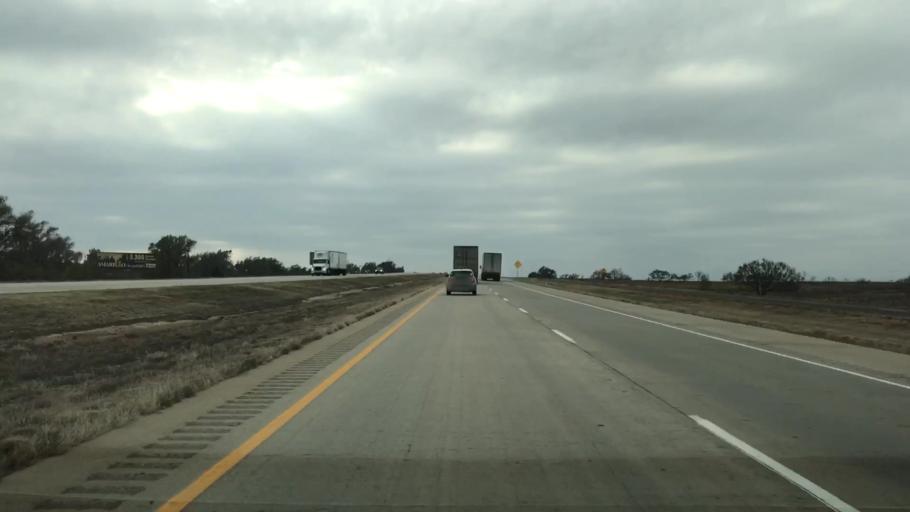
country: US
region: Texas
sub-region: Wheeler County
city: Shamrock
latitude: 35.2296
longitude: -100.2640
